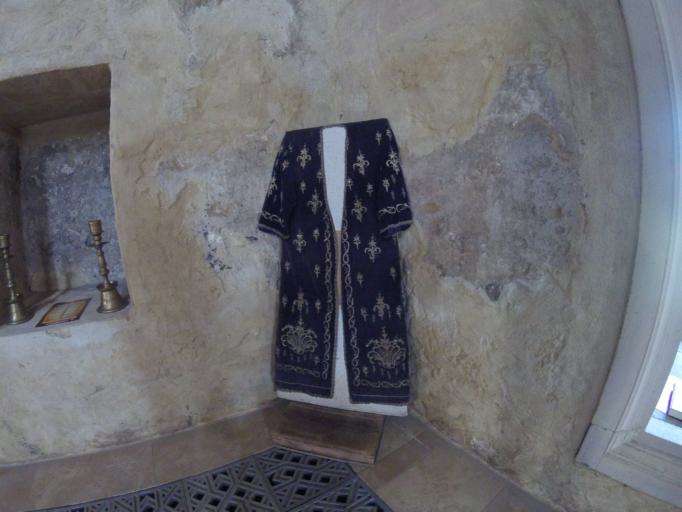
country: HU
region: Baranya
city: Siklos
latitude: 45.8514
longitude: 18.3001
